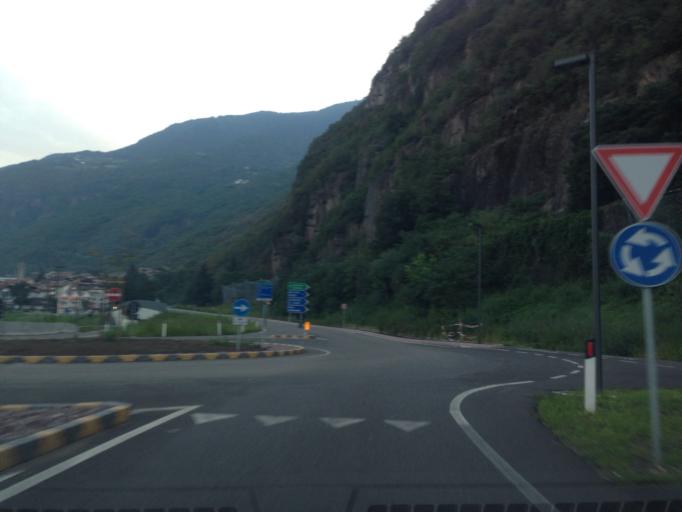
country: IT
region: Trentino-Alto Adige
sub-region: Bolzano
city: Pineta
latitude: 46.4324
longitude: 11.3463
